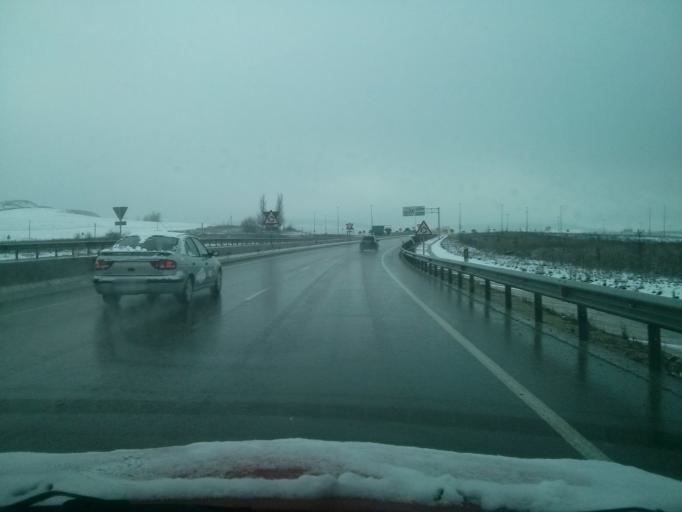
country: ES
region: Castille and Leon
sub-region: Provincia de Burgos
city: Sotragero
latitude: 42.3830
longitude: -3.6951
